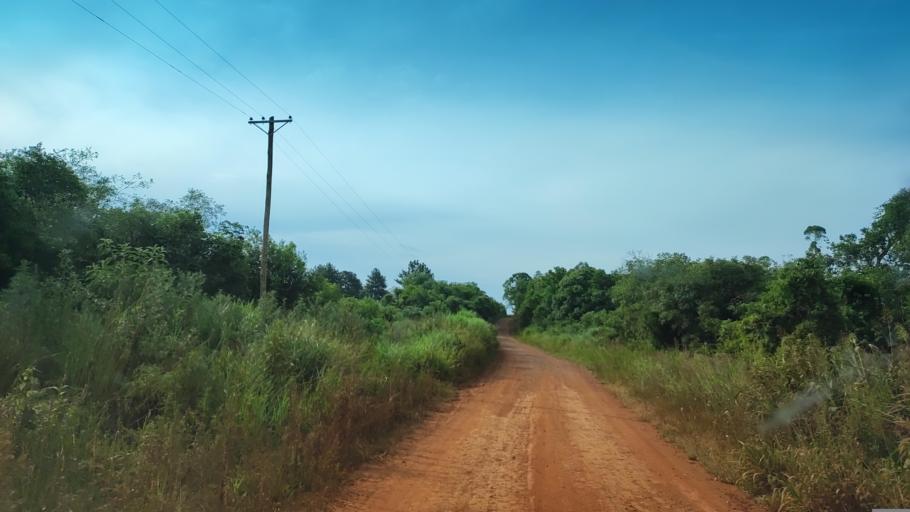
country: AR
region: Misiones
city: Gobernador Roca
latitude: -27.1818
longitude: -55.4961
